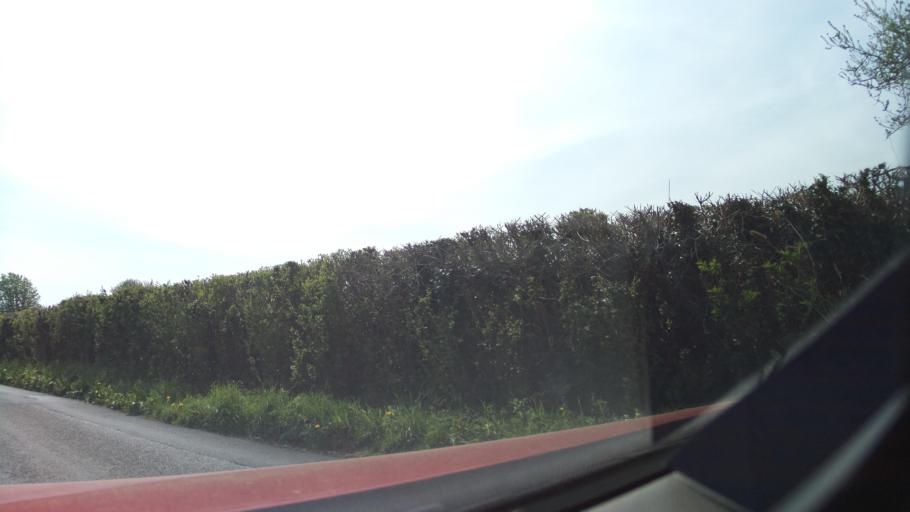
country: GB
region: England
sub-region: Somerset
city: Ilchester
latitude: 51.0180
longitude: -2.6347
